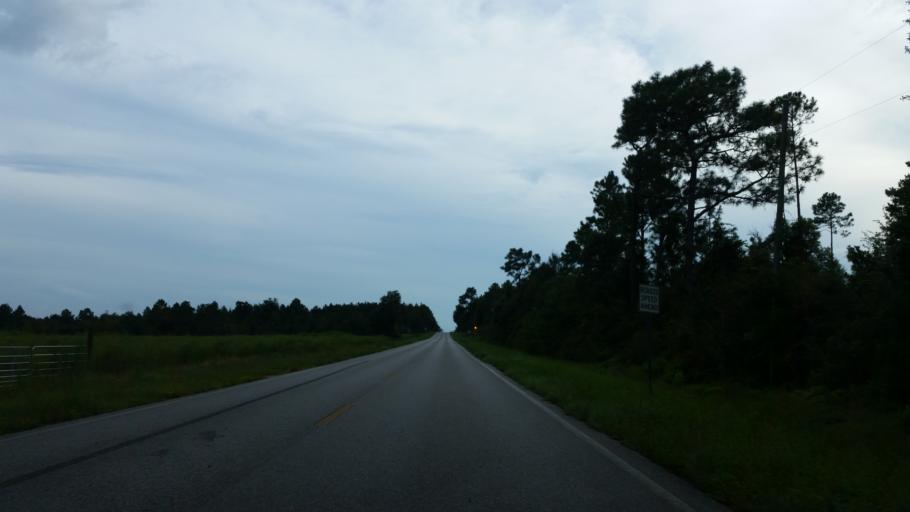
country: US
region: Florida
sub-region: Santa Rosa County
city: Point Baker
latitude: 30.6879
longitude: -86.9869
